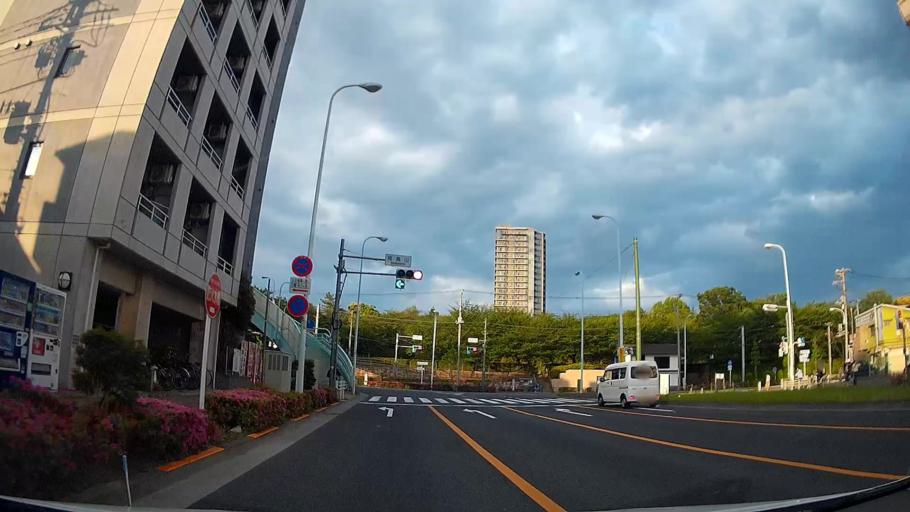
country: JP
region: Saitama
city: Kawaguchi
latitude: 35.7506
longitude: 139.7368
